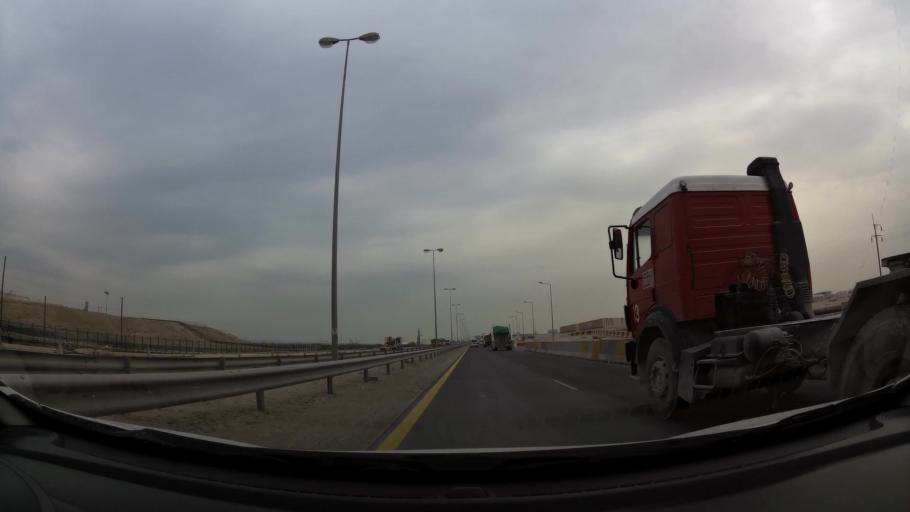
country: BH
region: Northern
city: Ar Rifa'
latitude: 26.1096
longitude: 50.5983
